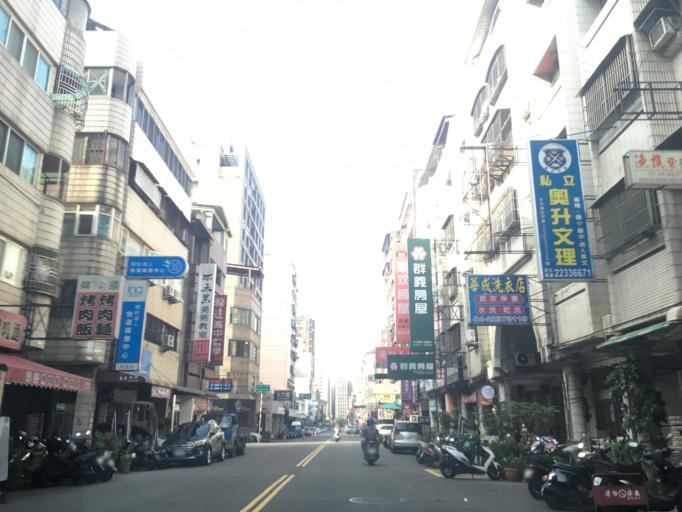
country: TW
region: Taiwan
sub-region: Taichung City
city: Taichung
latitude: 24.1709
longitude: 120.6815
